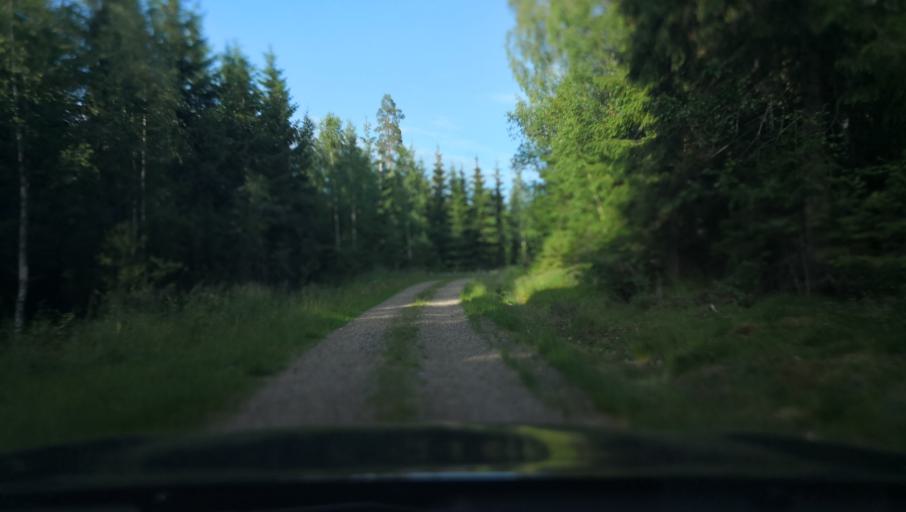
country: SE
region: Dalarna
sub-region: Ludvika Kommun
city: Ludvika
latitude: 60.0759
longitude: 15.2853
